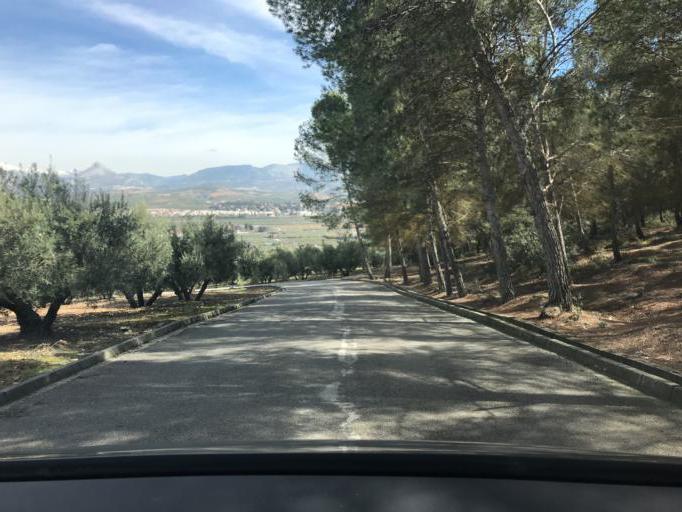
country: ES
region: Andalusia
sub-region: Provincia de Granada
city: Atarfe
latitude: 37.2499
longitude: -3.6793
